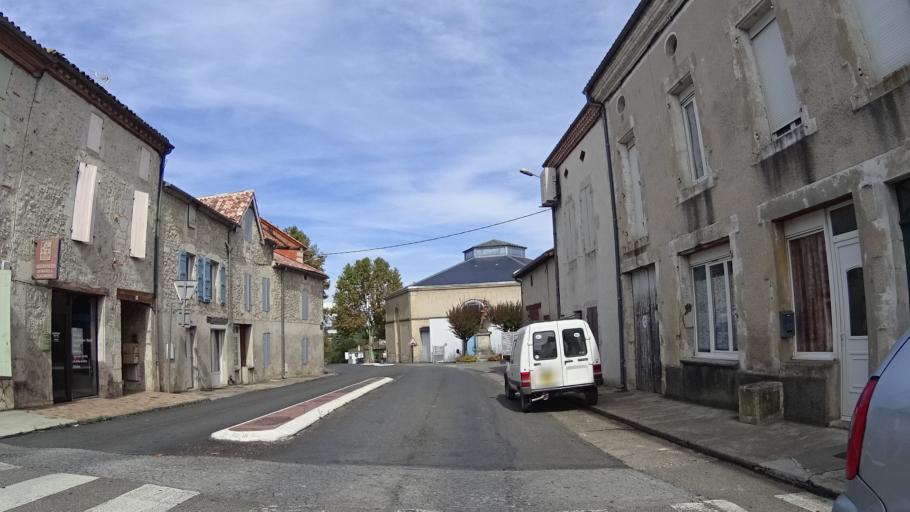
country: FR
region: Aquitaine
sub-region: Departement du Lot-et-Garonne
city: Astaffort
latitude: 44.0625
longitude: 0.6507
